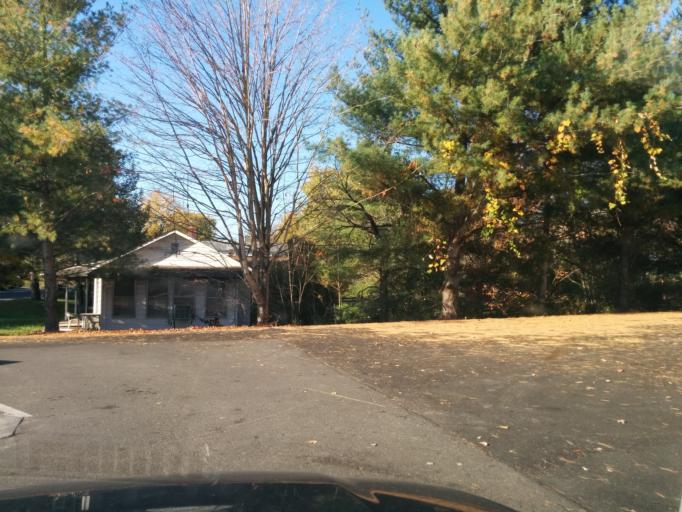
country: US
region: Virginia
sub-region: City of Lexington
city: Lexington
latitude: 37.7785
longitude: -79.4381
